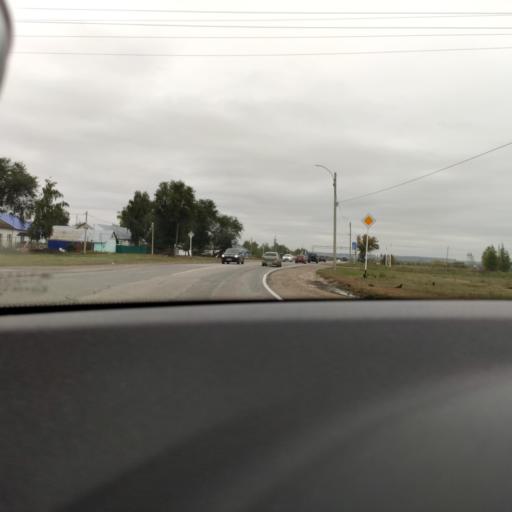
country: RU
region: Samara
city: Krasnyy Yar
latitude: 53.4813
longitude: 50.3921
